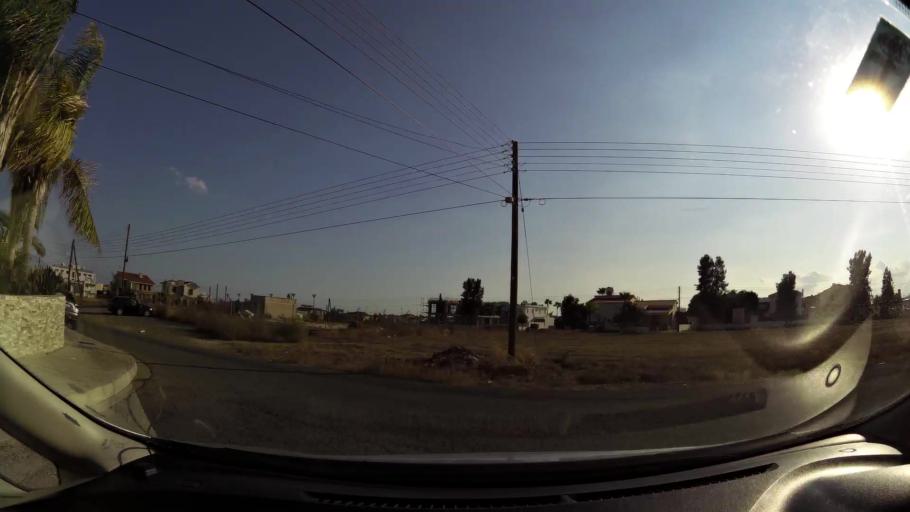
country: CY
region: Larnaka
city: Aradippou
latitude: 34.9432
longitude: 33.5991
